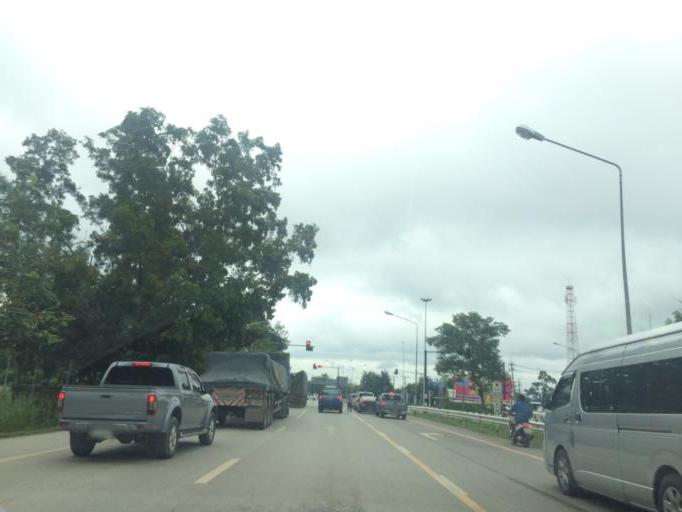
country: TH
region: Chiang Rai
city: Chiang Rai
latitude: 19.8487
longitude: 99.8078
